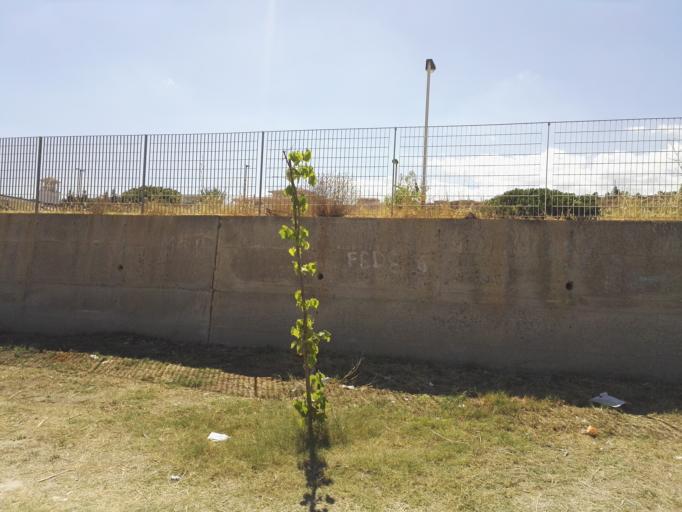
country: IT
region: Calabria
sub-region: Provincia di Catanzaro
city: Santa Caterina dello Ionio Marina
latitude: 38.5309
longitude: 16.5713
